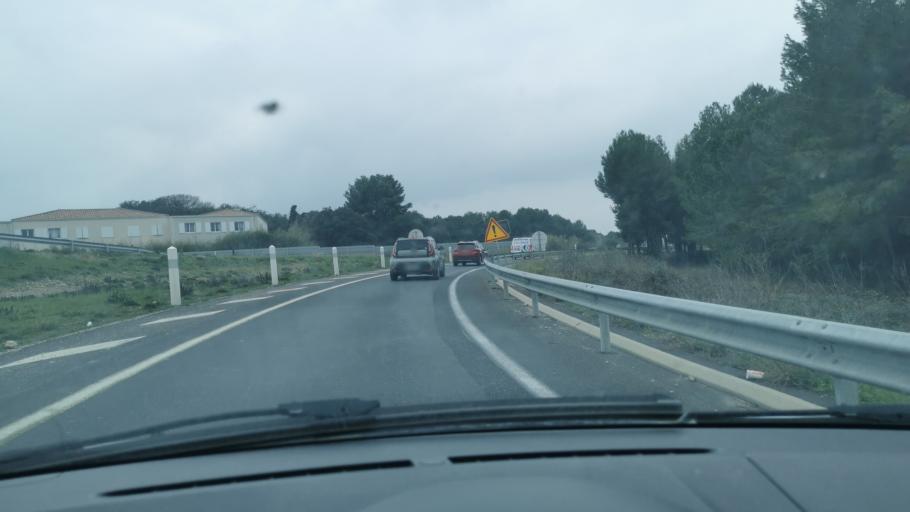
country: FR
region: Languedoc-Roussillon
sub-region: Departement de l'Herault
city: Saint-Jean-de-Vedas
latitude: 43.5659
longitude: 3.8351
